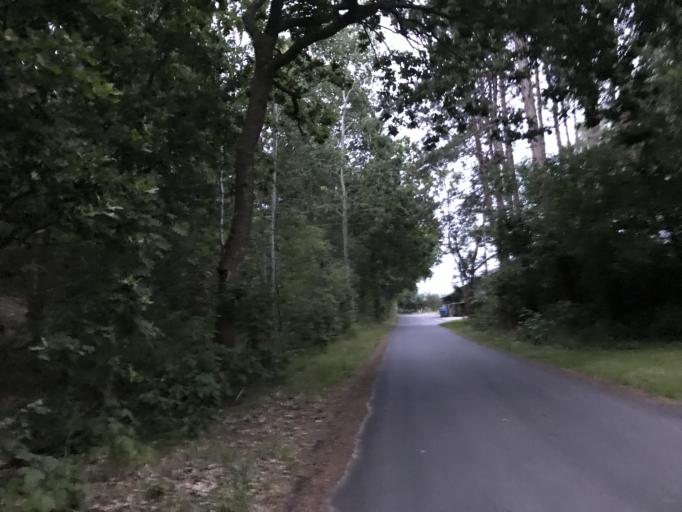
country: DK
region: South Denmark
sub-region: Faaborg-Midtfyn Kommune
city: Faaborg
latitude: 54.9356
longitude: 10.2466
